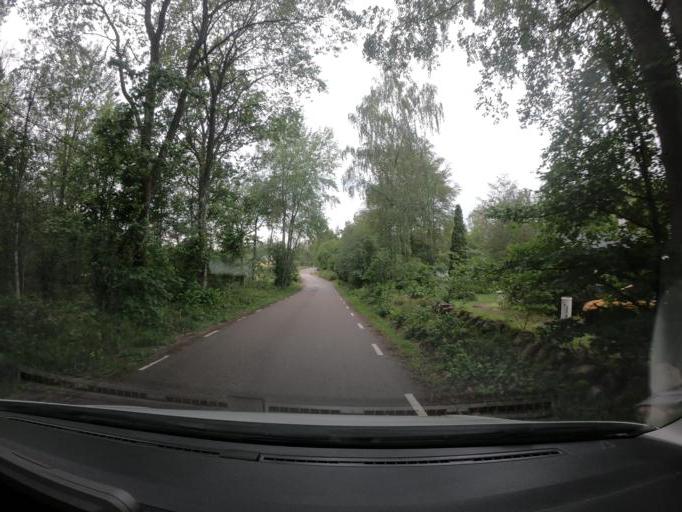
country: SE
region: Skane
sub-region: Klippans Kommun
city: Klippan
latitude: 56.2671
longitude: 13.1433
